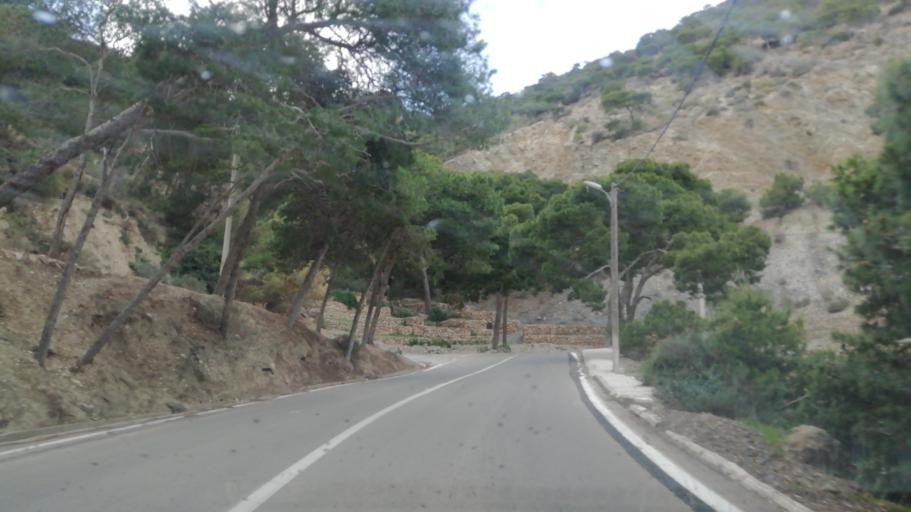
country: DZ
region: Oran
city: Oran
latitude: 35.7063
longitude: -0.6648
